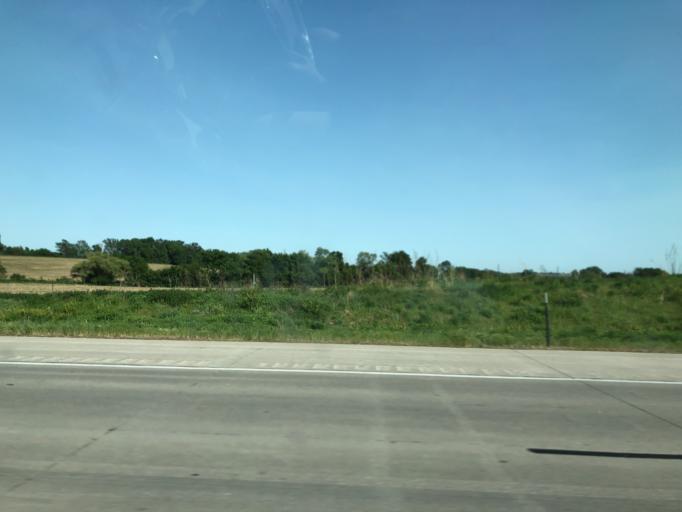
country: US
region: Nebraska
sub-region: Saunders County
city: Ashland
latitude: 40.9459
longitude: -96.4232
